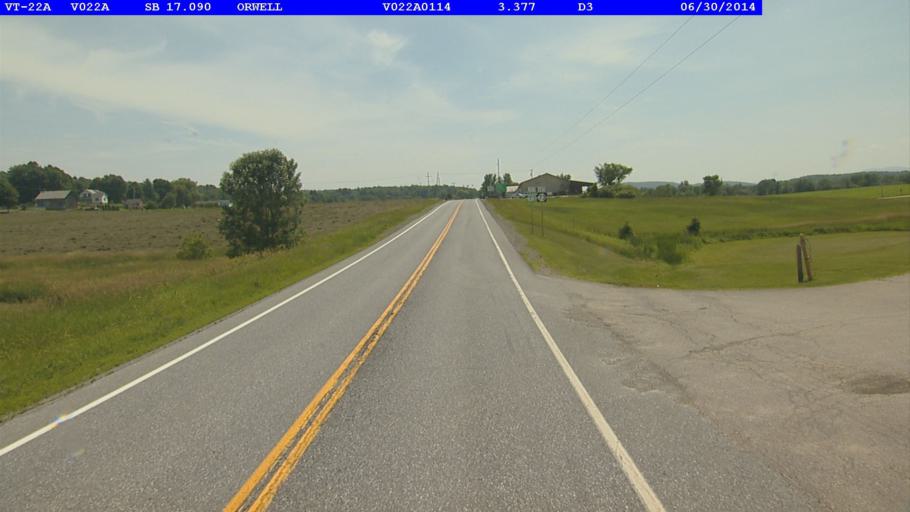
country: US
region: New York
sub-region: Essex County
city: Ticonderoga
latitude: 43.8057
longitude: -73.3048
